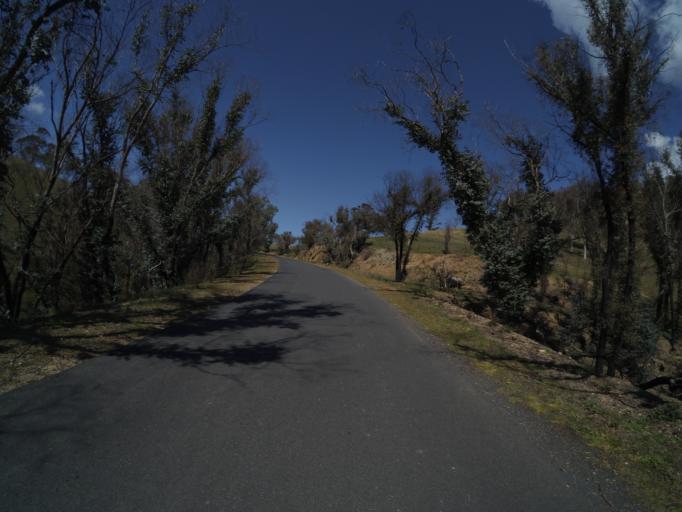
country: AU
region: New South Wales
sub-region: Yass Valley
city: Murrumbateman
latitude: -35.0913
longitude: 148.8473
